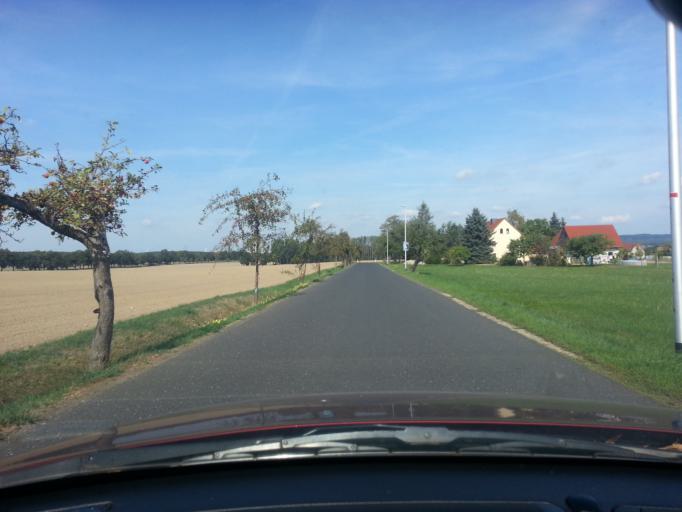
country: DE
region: Saxony
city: Reichenbach
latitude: 51.1053
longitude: 14.8328
